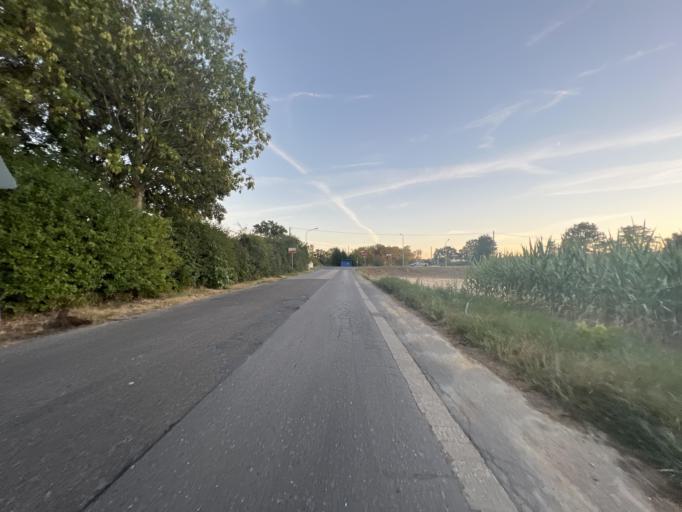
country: DE
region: North Rhine-Westphalia
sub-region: Regierungsbezirk Koln
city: Langerwehe
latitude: 50.8070
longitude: 6.4179
